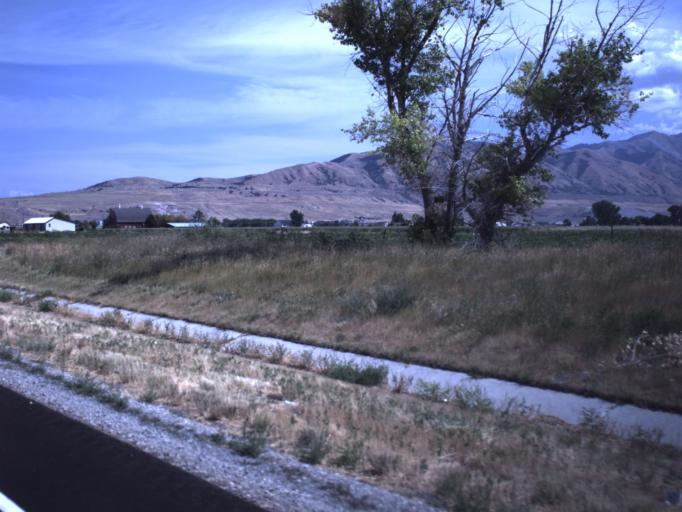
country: US
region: Utah
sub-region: Box Elder County
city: Garland
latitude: 41.7853
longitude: -112.1312
